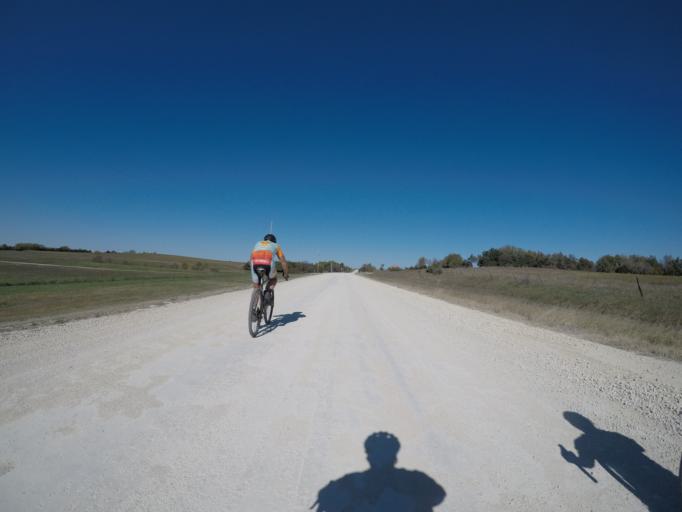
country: US
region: Kansas
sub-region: Wabaunsee County
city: Alma
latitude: 39.0672
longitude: -96.3539
